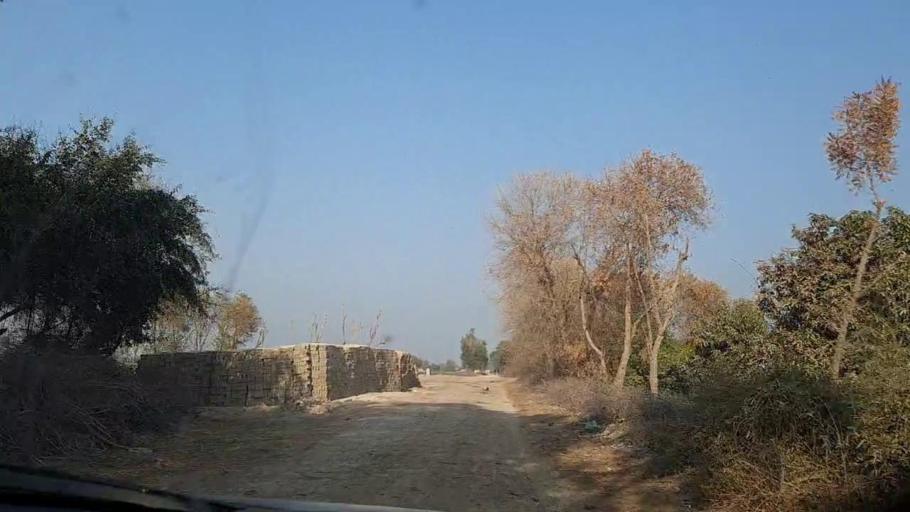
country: PK
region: Sindh
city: Moro
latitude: 26.7957
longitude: 67.9431
